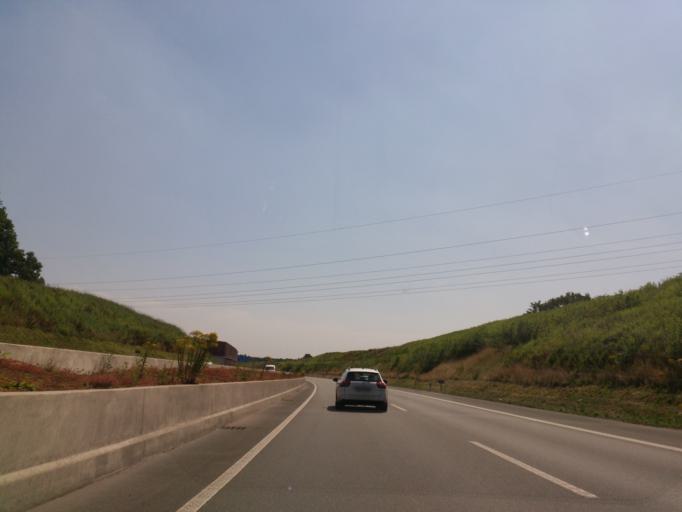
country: DE
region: North Rhine-Westphalia
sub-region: Regierungsbezirk Detmold
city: Verl
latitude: 51.9507
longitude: 8.5068
